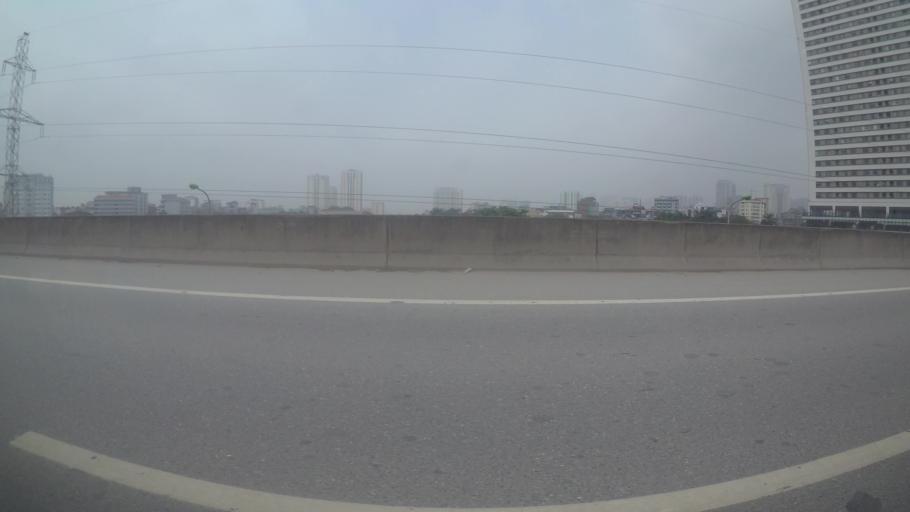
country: VN
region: Ha Noi
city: Cau Dien
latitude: 21.0258
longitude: 105.7787
